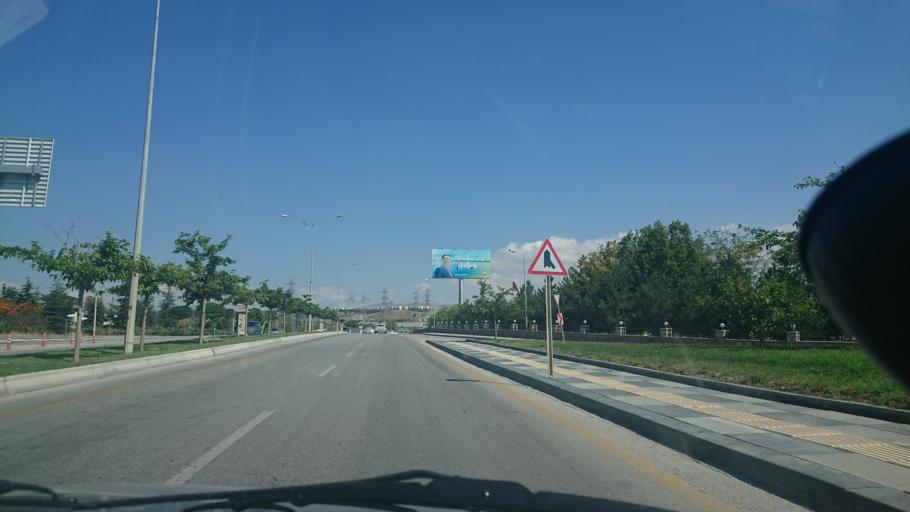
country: TR
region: Ankara
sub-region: Goelbasi
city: Golbasi
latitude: 39.8035
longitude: 32.8058
